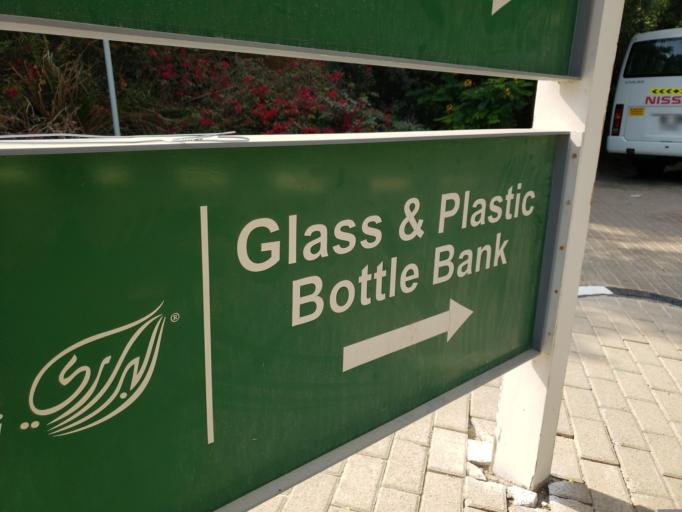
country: AE
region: Dubai
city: Dubai
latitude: 25.0948
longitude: 55.3111
